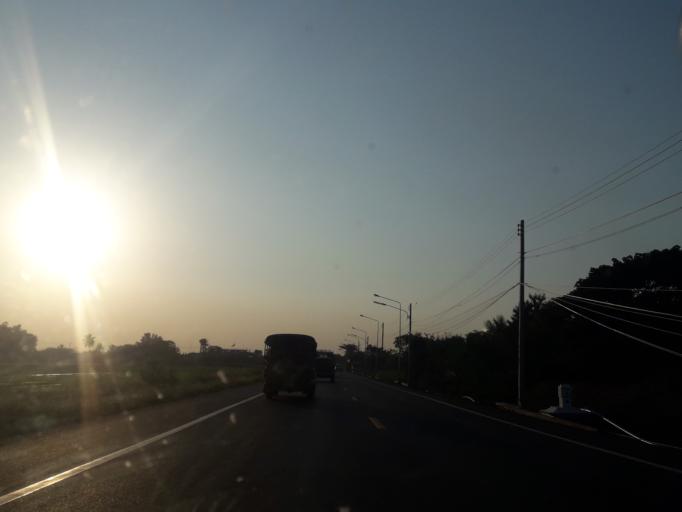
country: TH
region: Pathum Thani
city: Nong Suea
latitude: 14.1318
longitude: 100.7594
